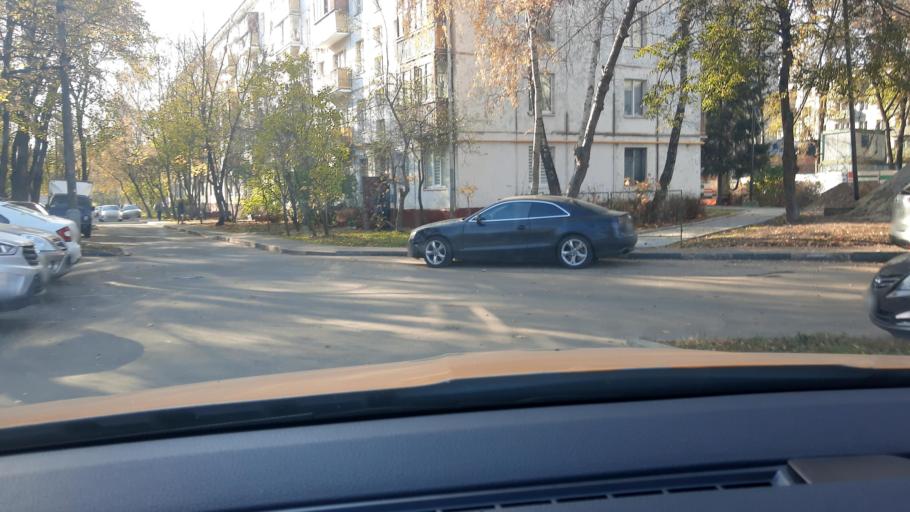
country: RU
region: Moscow
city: Kuz'minki
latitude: 55.7039
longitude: 37.7881
